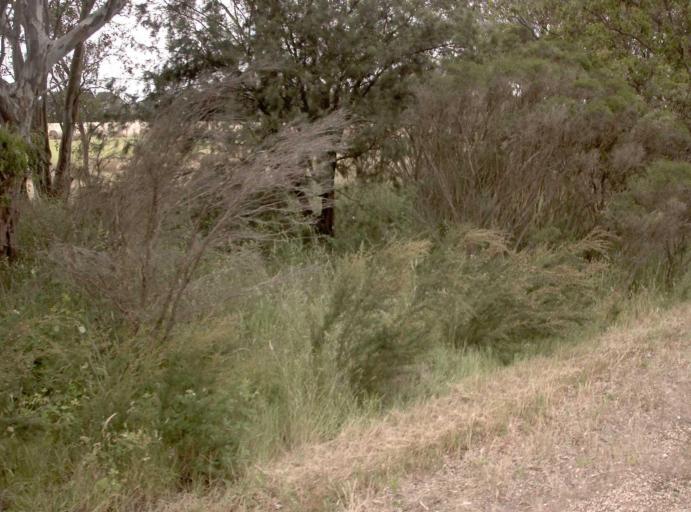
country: AU
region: Victoria
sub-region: Wellington
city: Sale
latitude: -37.9693
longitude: 147.1412
